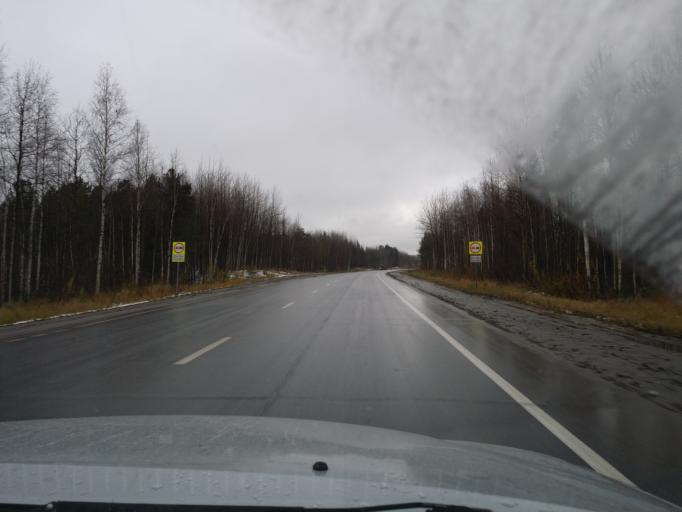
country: RU
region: Khanty-Mansiyskiy Avtonomnyy Okrug
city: Megion
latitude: 61.1002
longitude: 76.0573
